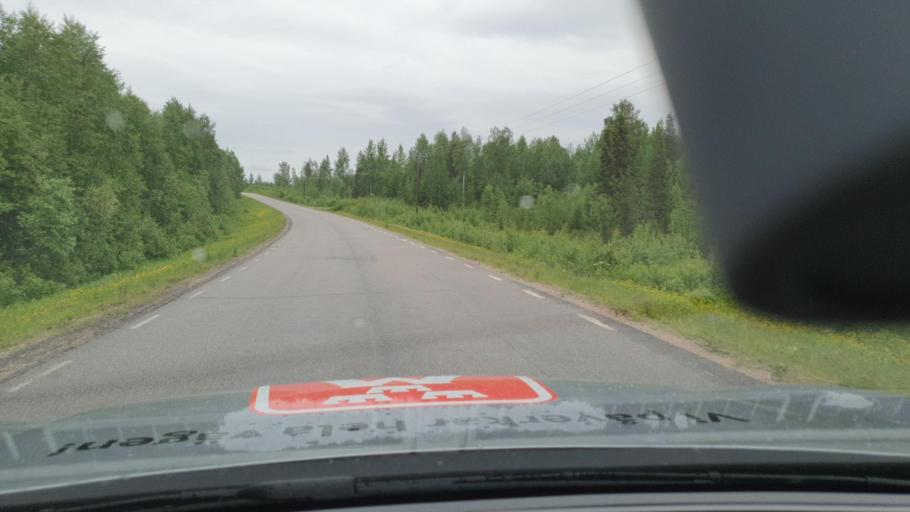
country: SE
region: Norrbotten
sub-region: Pajala Kommun
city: Pajala
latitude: 66.7524
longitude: 23.1605
